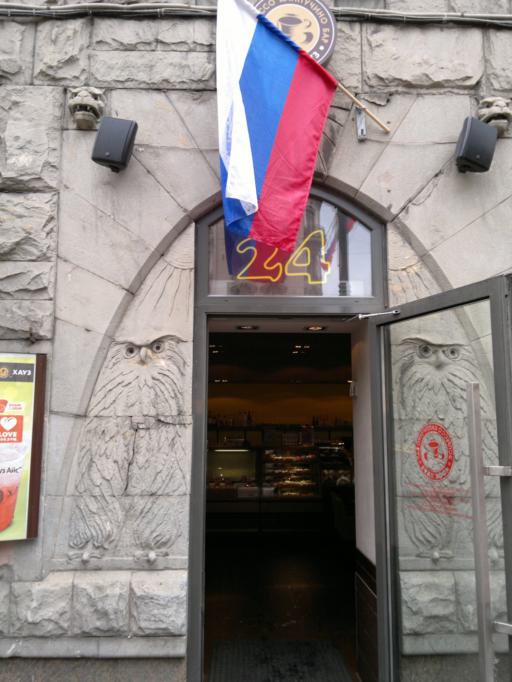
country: RU
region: St.-Petersburg
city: Centralniy
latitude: 59.9329
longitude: 30.3471
